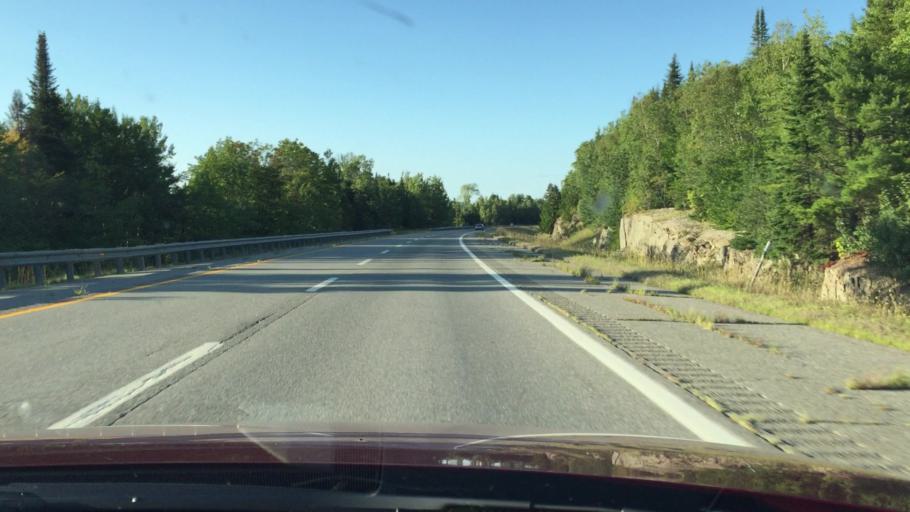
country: US
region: Maine
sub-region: Penobscot County
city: Patten
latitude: 45.8381
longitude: -68.4331
